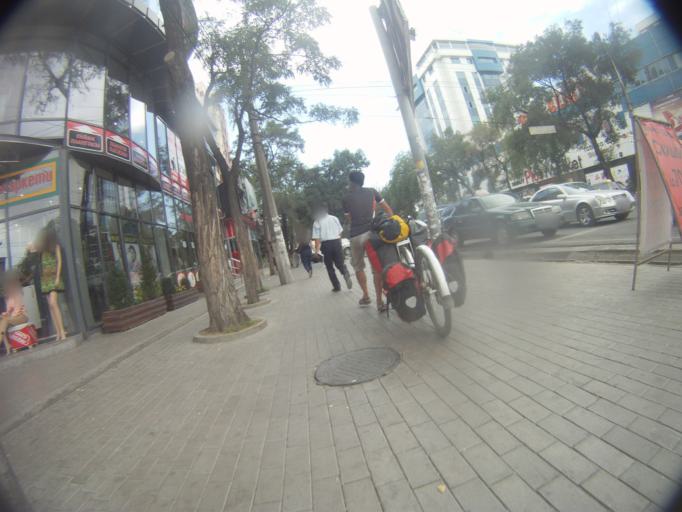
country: KG
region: Chuy
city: Bishkek
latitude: 42.8571
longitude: 74.6101
